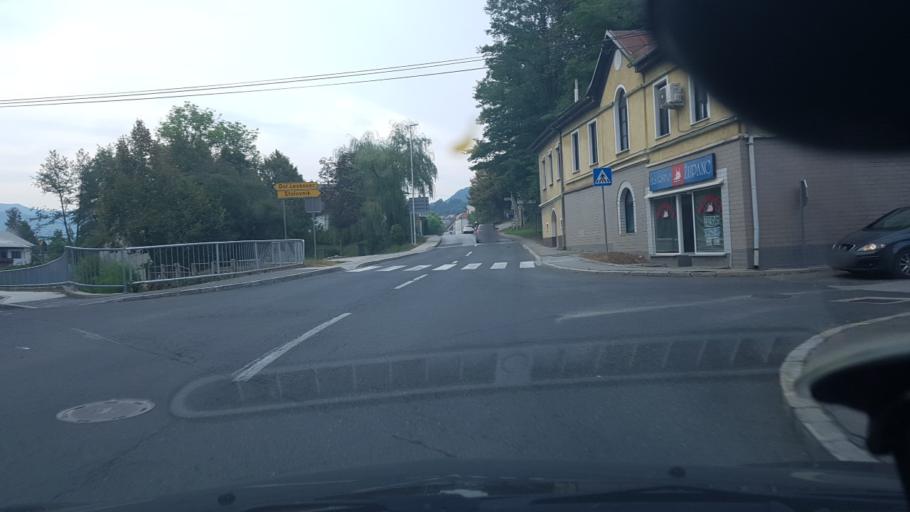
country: SI
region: Krsko
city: Senovo
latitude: 45.9942
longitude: 15.4755
